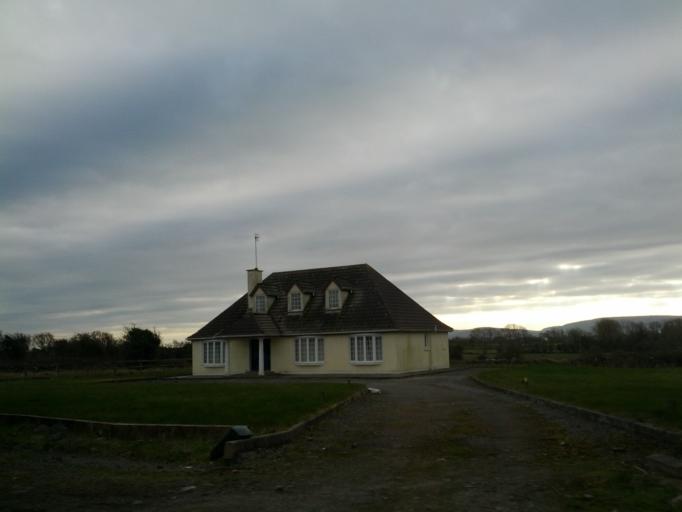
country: IE
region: Connaught
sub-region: County Galway
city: Gort
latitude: 53.1628
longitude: -8.8764
